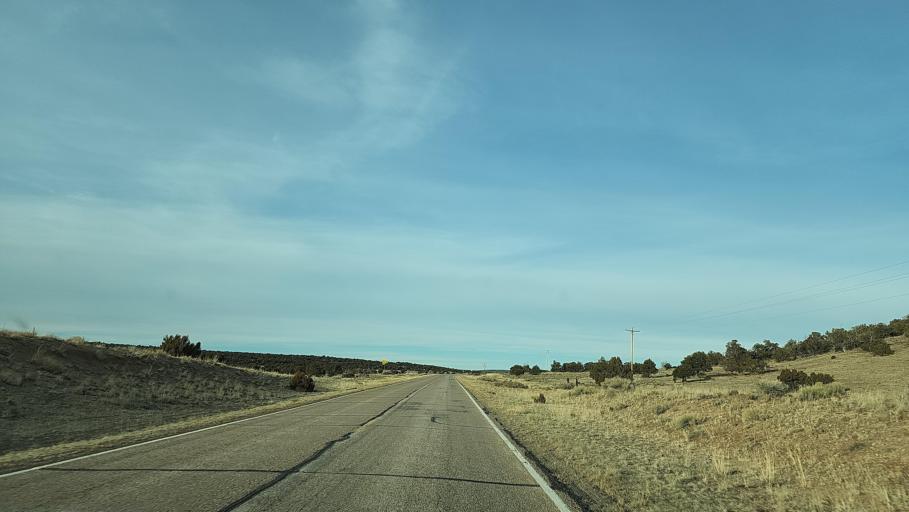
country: US
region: New Mexico
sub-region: Catron County
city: Reserve
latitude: 34.3952
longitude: -108.4457
